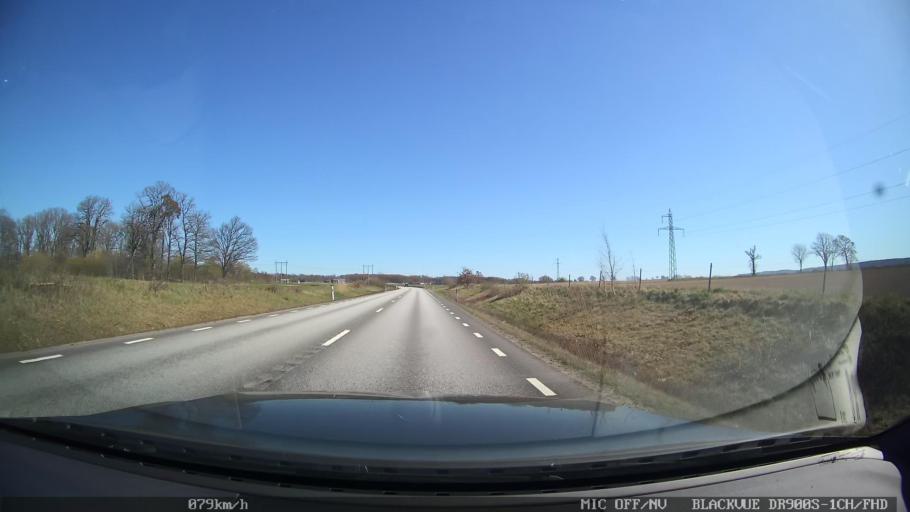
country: SE
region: Skane
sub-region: Klippans Kommun
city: Klippan
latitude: 56.1166
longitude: 13.1360
